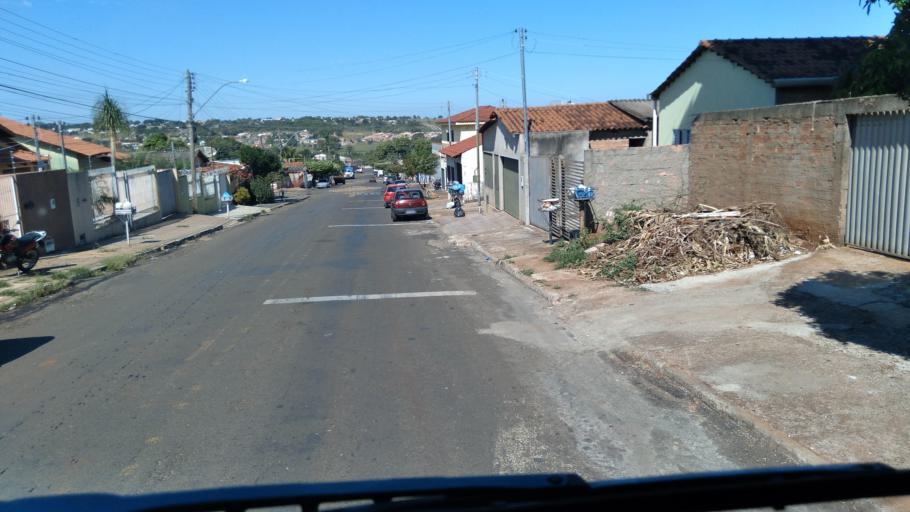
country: BR
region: Goias
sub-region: Mineiros
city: Mineiros
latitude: -17.5704
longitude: -52.5655
